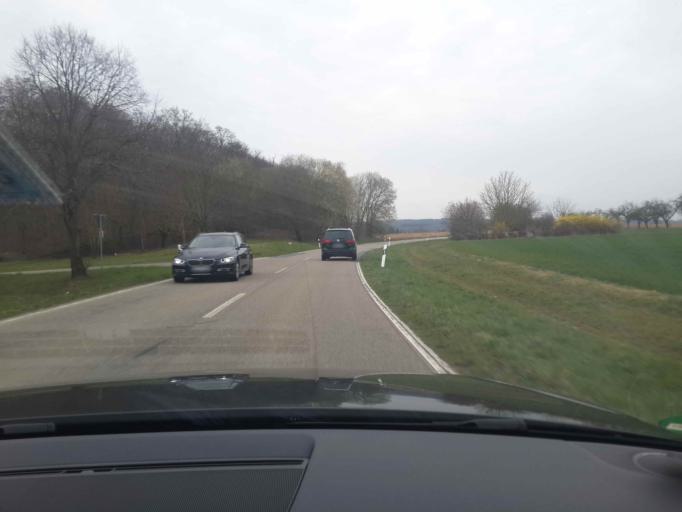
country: DE
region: Baden-Wuerttemberg
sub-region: Regierungsbezirk Stuttgart
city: Oedheim
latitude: 49.2300
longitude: 9.2701
